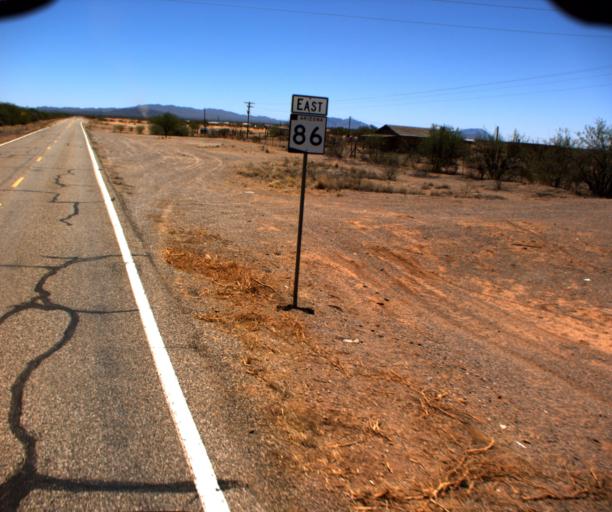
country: US
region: Arizona
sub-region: Pima County
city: Ajo
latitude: 32.1855
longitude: -112.3724
